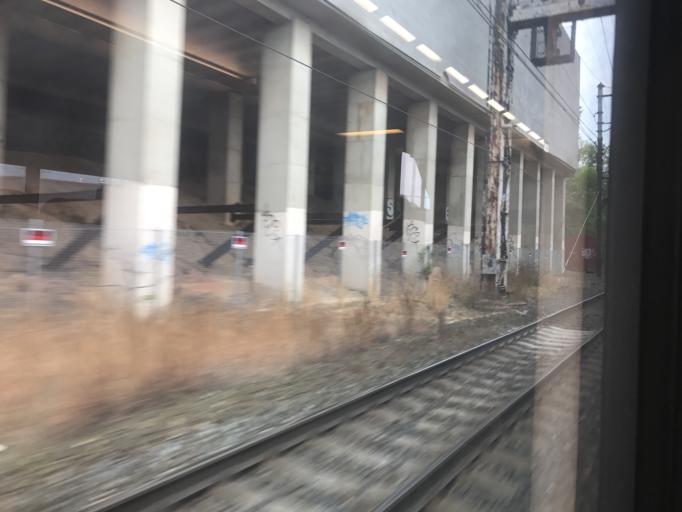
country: US
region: Maryland
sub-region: Prince George's County
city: Mount Rainier
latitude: 38.9125
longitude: -76.9958
